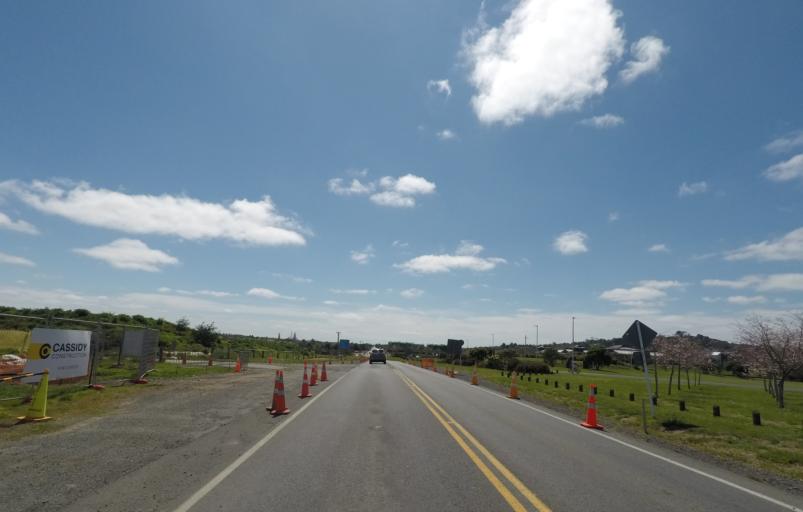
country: NZ
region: Auckland
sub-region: Auckland
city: Manukau City
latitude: -36.9605
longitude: 174.9078
